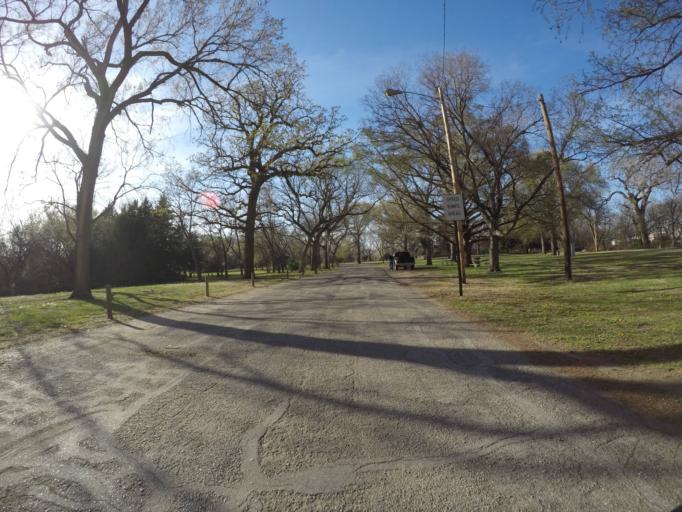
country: US
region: Kansas
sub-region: Saline County
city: Salina
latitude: 38.8660
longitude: -97.6135
